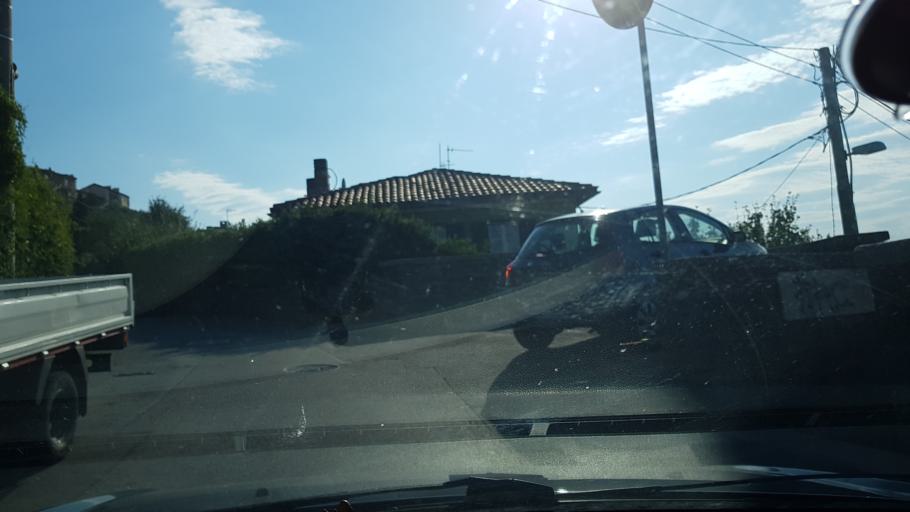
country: IT
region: Friuli Venezia Giulia
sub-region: Provincia di Trieste
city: Trieste
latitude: 45.6444
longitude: 13.8003
